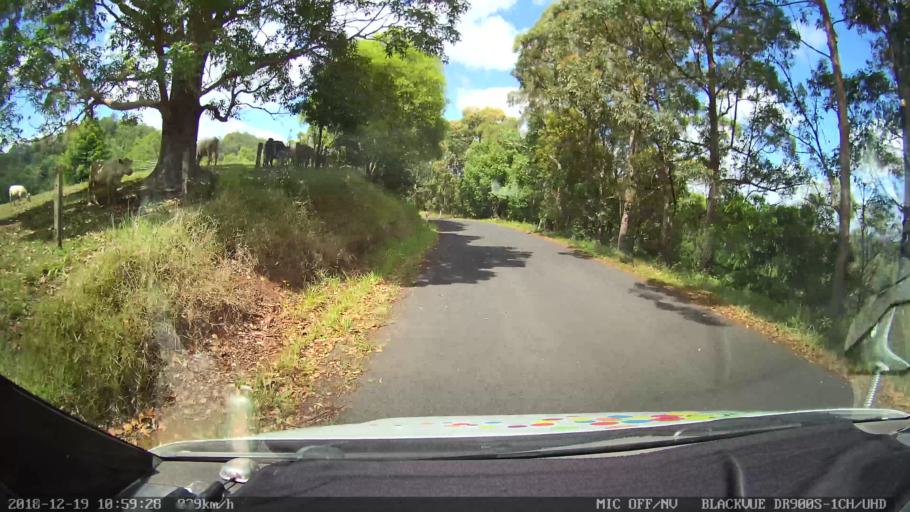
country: AU
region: New South Wales
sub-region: Lismore Municipality
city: Nimbin
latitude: -28.5965
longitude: 153.2620
